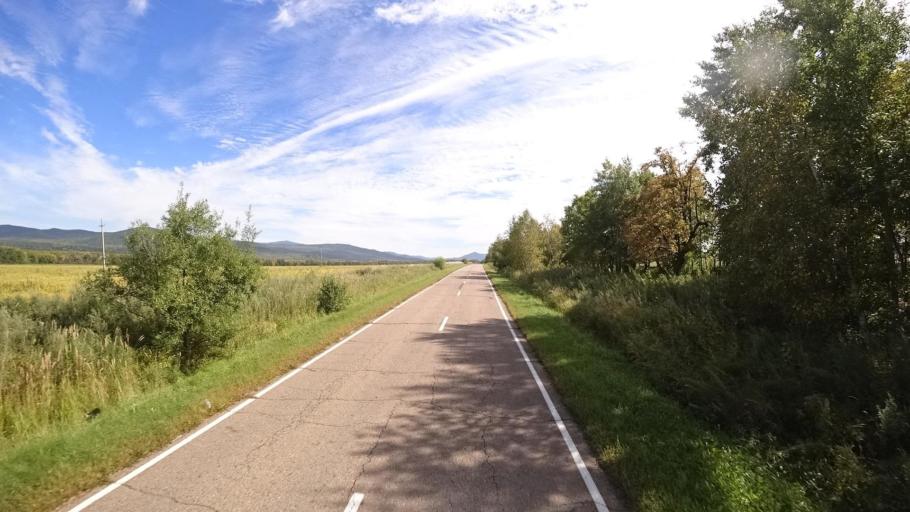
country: RU
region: Primorskiy
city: Yakovlevka
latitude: 44.4181
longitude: 133.5817
